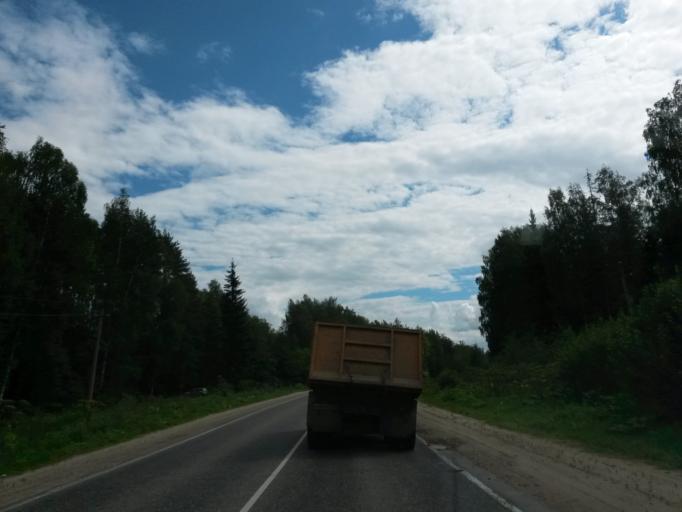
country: RU
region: Ivanovo
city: Novo-Talitsy
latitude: 57.0539
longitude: 40.7327
